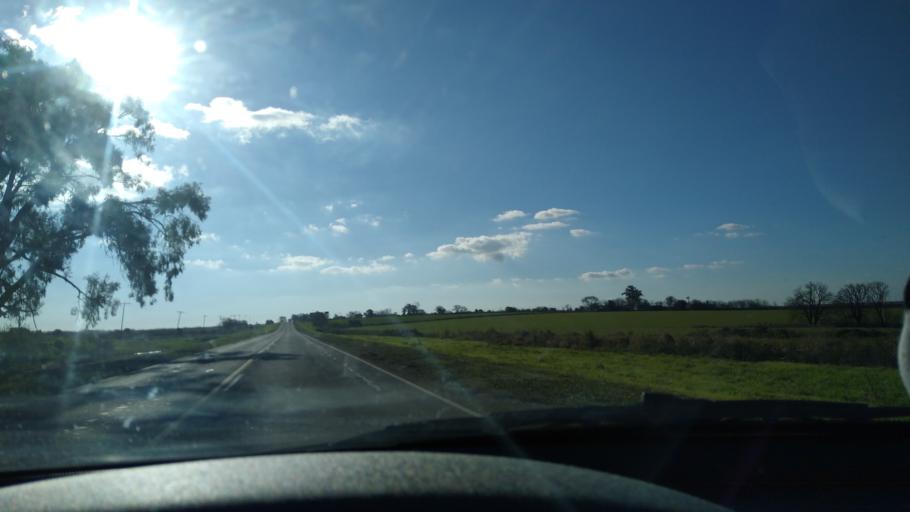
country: AR
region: Entre Rios
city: Diamante
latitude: -32.1119
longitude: -60.5758
